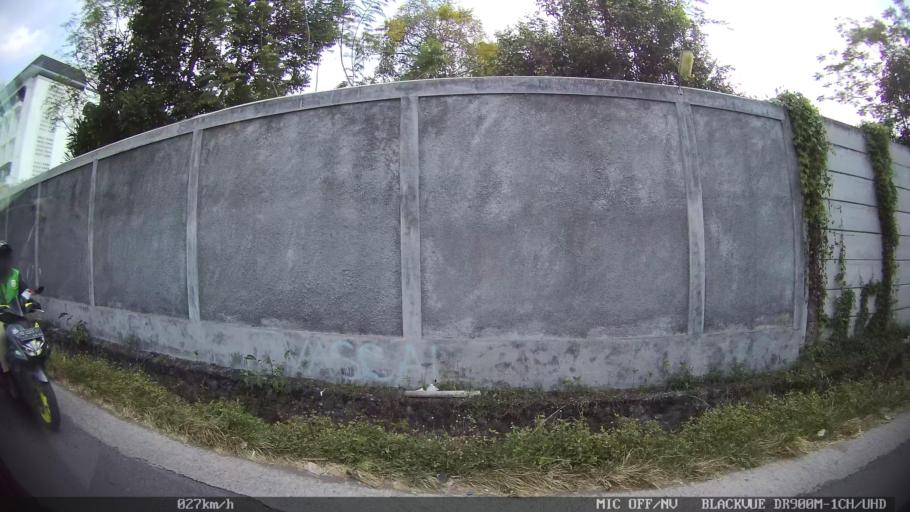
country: ID
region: Daerah Istimewa Yogyakarta
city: Depok
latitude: -7.7973
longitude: 110.4056
